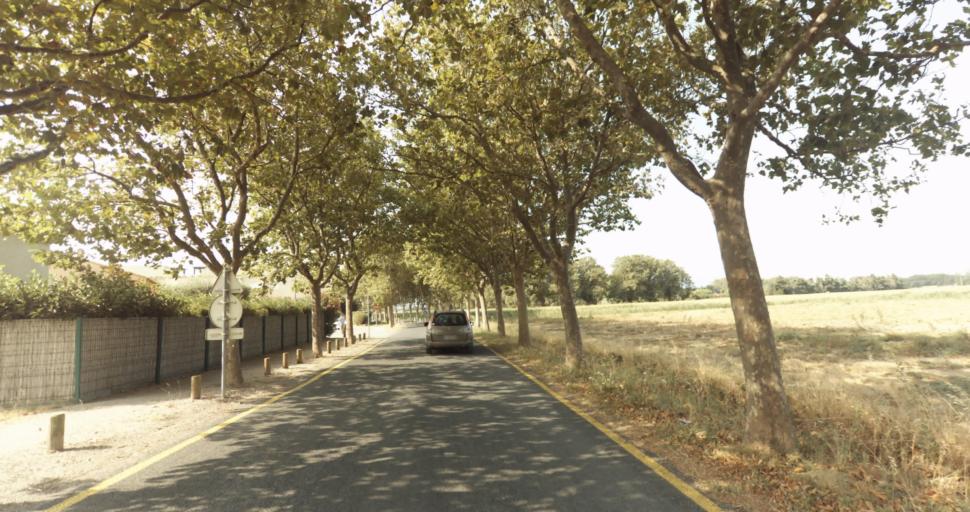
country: FR
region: Languedoc-Roussillon
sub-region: Departement des Pyrenees-Orientales
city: Latour-Bas-Elne
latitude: 42.5995
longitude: 3.0324
